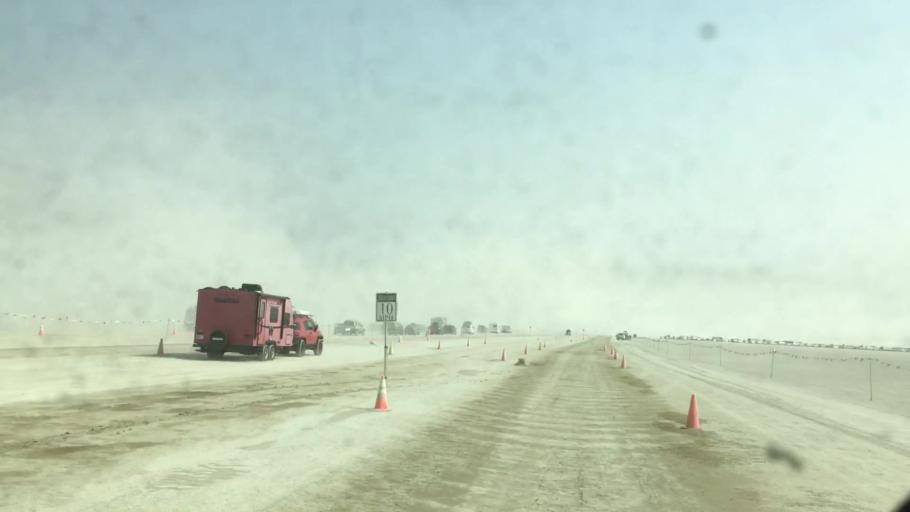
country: US
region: Nevada
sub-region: Pershing County
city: Lovelock
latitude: 40.7615
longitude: -119.2514
